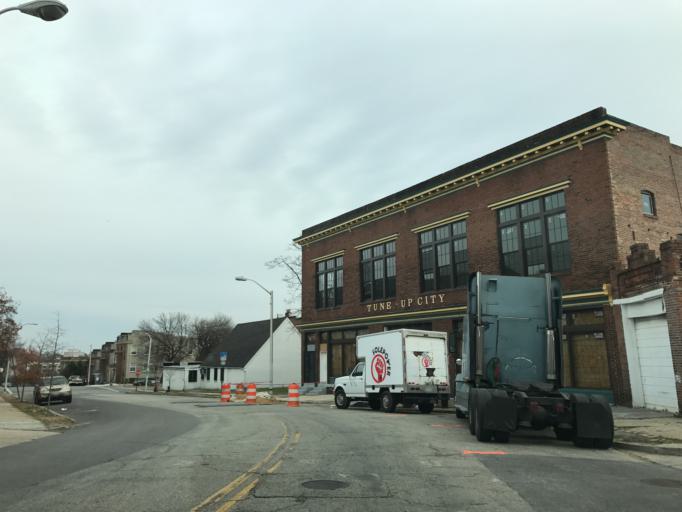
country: US
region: Maryland
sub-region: City of Baltimore
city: Baltimore
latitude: 39.3144
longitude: -76.6310
